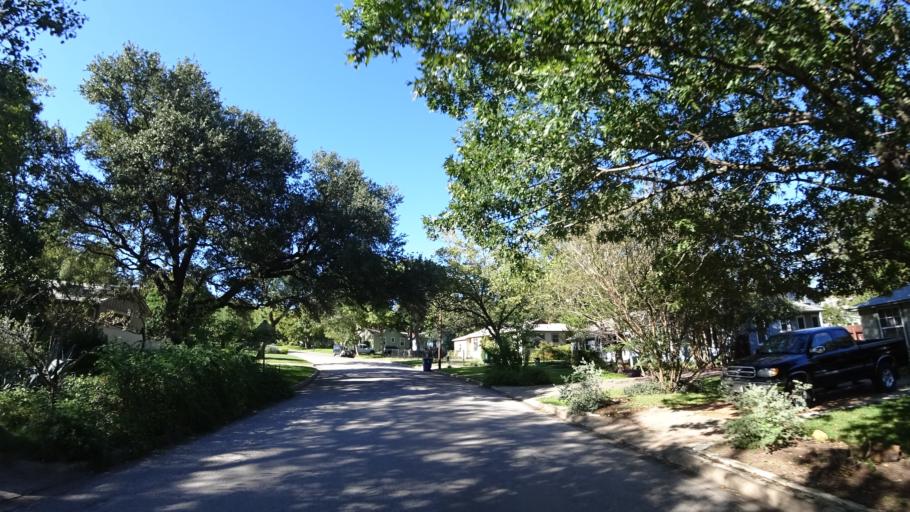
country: US
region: Texas
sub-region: Travis County
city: West Lake Hills
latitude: 30.3328
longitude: -97.7584
